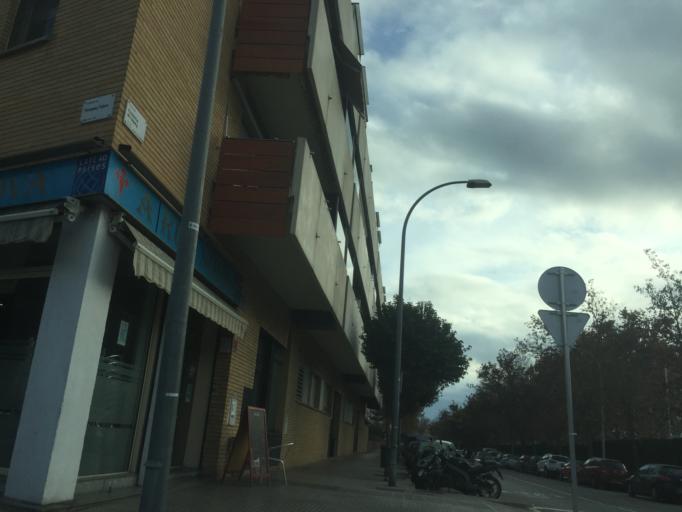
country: ES
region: Catalonia
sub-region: Provincia de Barcelona
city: El Prat de Llobregat
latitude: 41.3215
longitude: 2.0837
